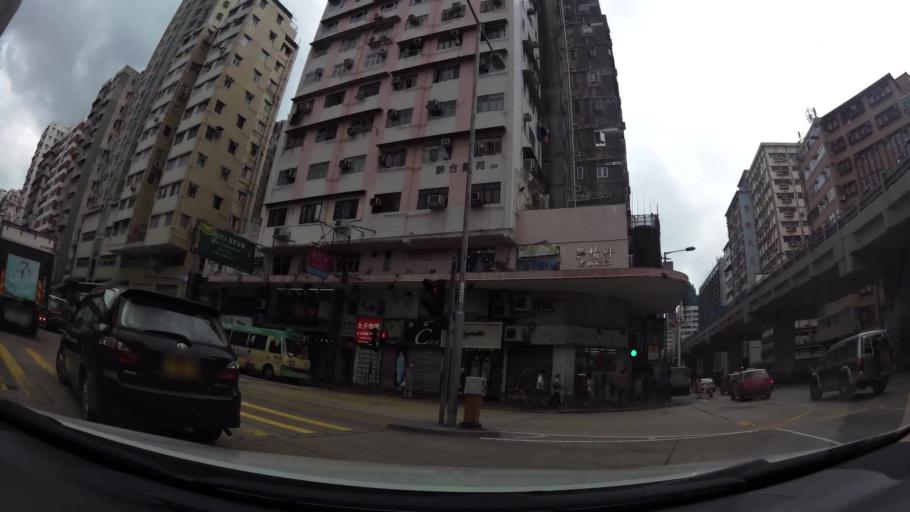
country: HK
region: Sham Shui Po
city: Sham Shui Po
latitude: 22.3241
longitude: 114.1709
